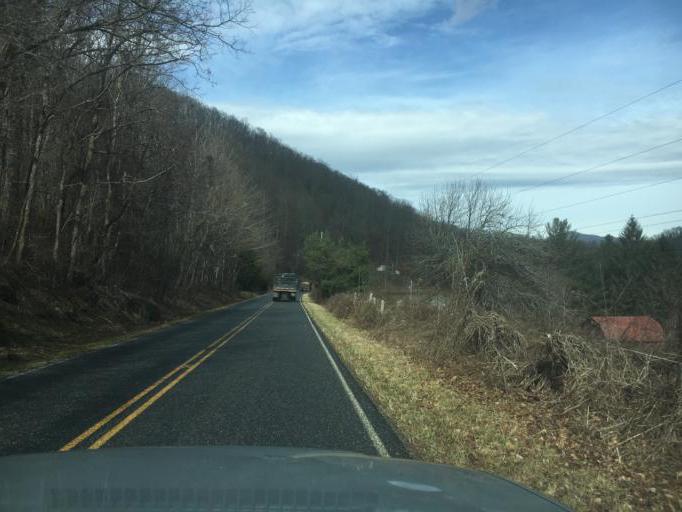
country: US
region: North Carolina
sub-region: Haywood County
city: Canton
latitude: 35.3946
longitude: -82.8148
